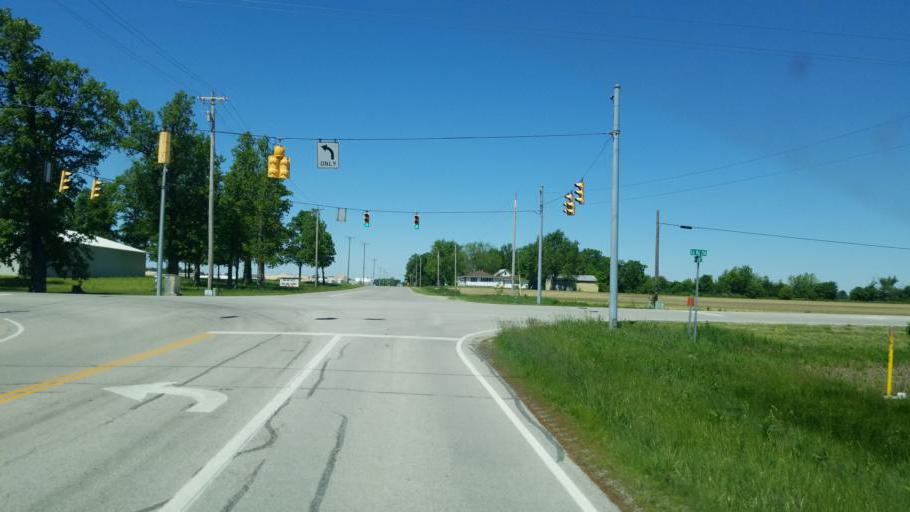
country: US
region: Ohio
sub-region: Shelby County
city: Anna
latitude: 40.3806
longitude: -84.1711
